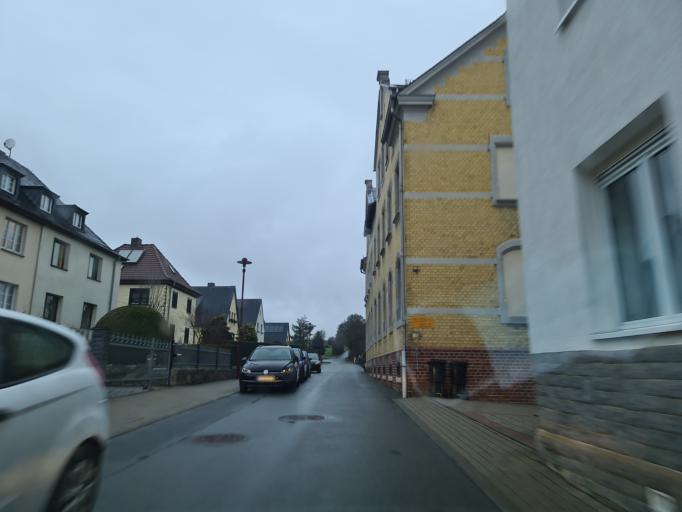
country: DE
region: Saxony
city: Syrau
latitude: 50.4963
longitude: 12.0896
